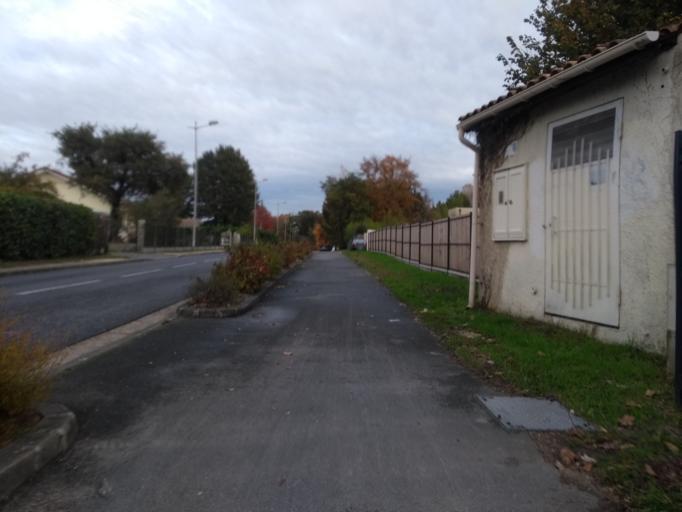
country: FR
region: Aquitaine
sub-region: Departement de la Gironde
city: Canejan
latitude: 44.7664
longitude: -0.6369
